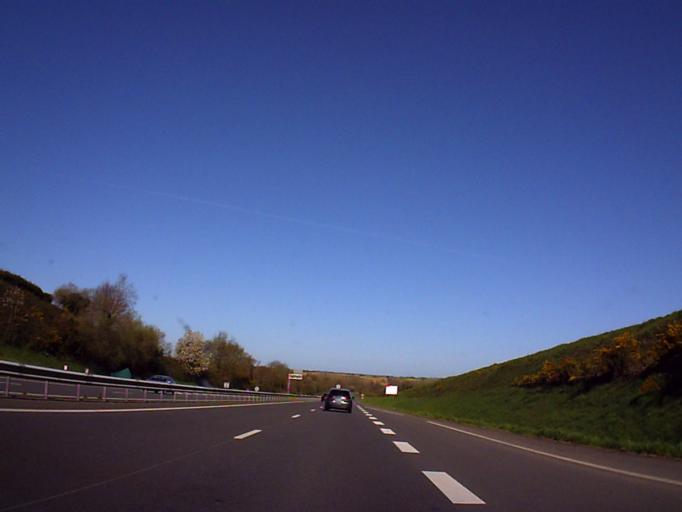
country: FR
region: Brittany
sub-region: Departement des Cotes-d'Armor
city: Broons
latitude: 48.3220
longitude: -2.2531
